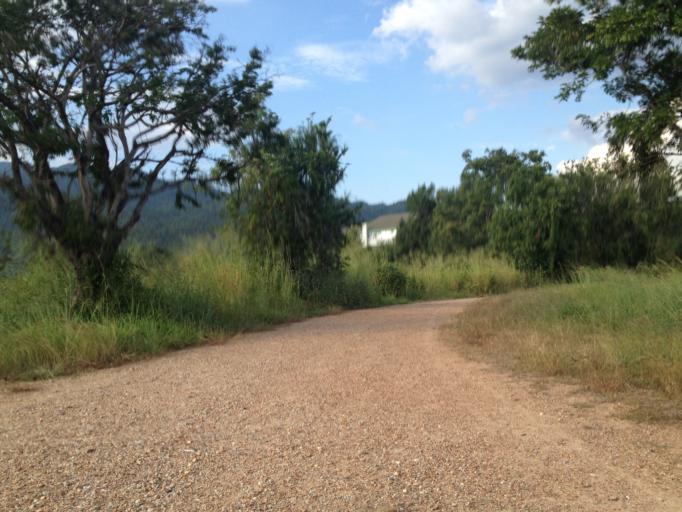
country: TH
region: Chiang Mai
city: Chiang Mai
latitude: 18.7591
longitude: 98.9362
